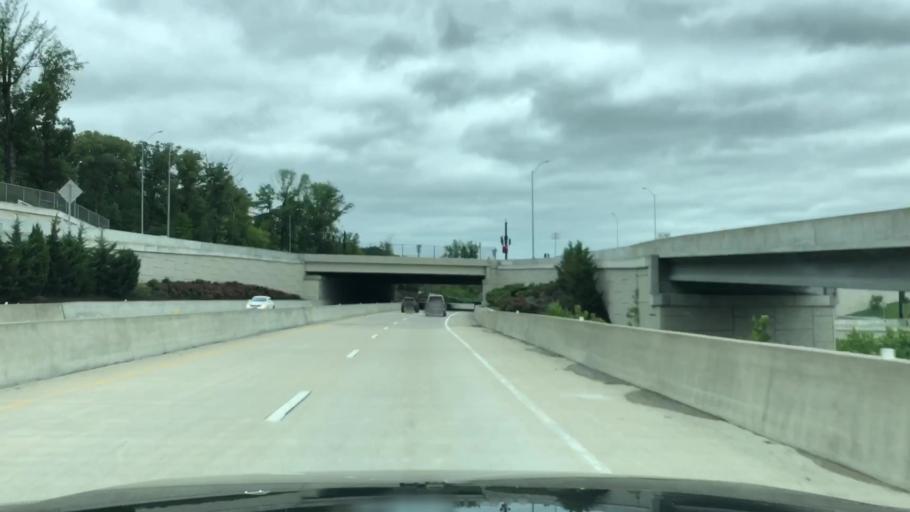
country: US
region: Missouri
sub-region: Saint Louis County
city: Town and Country
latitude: 38.6616
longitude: -90.5031
